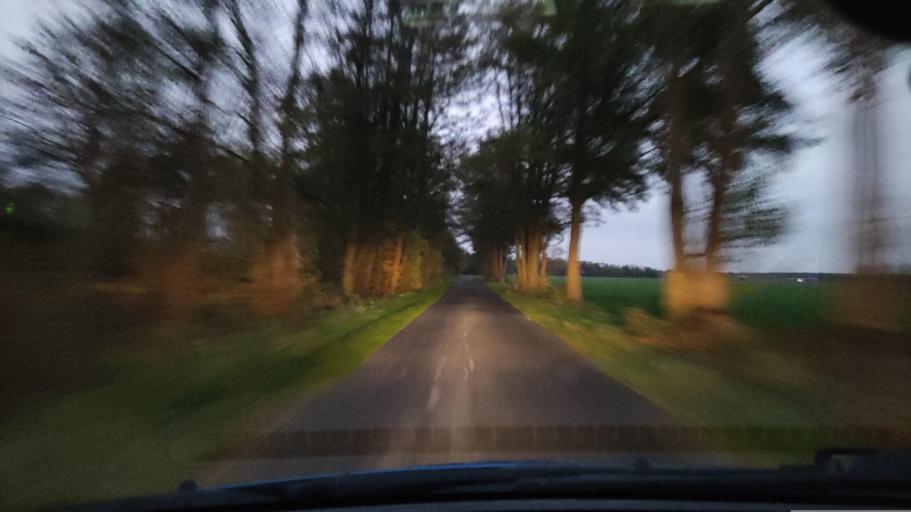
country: DE
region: Mecklenburg-Vorpommern
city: Domitz
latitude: 53.1609
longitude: 11.2126
